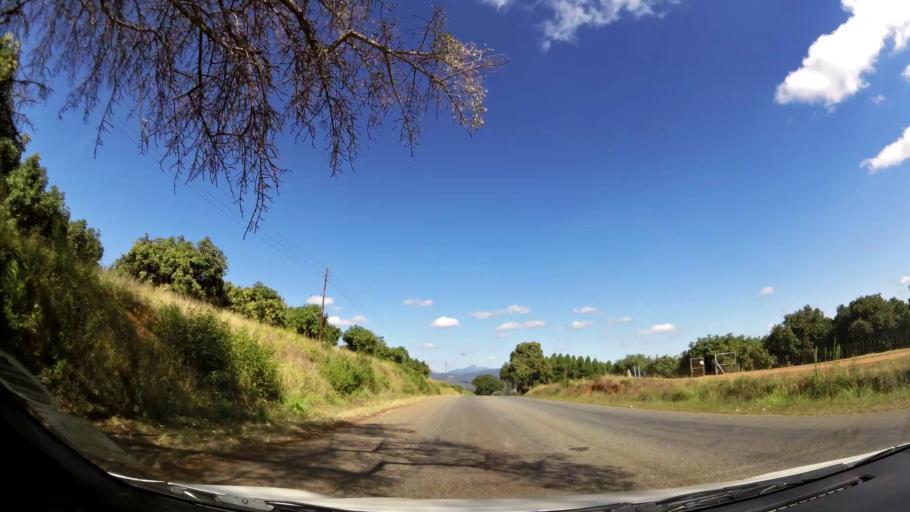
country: ZA
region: Limpopo
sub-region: Mopani District Municipality
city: Tzaneen
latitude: -23.8063
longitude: 30.1778
